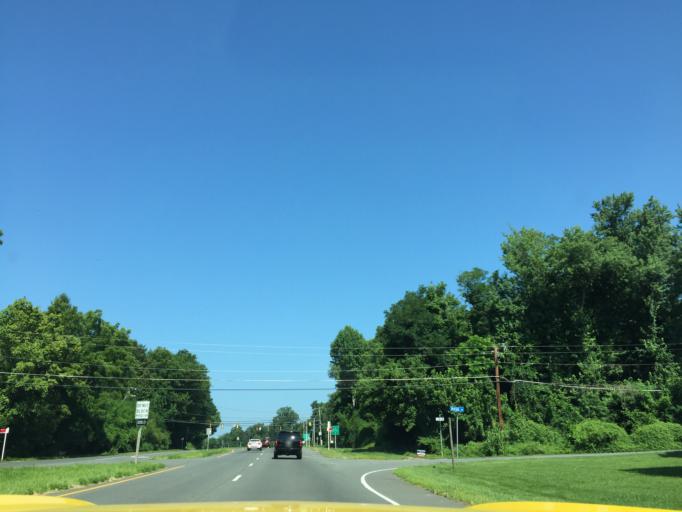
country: US
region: Maryland
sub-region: Montgomery County
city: Brookmont
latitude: 38.9427
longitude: -77.1419
